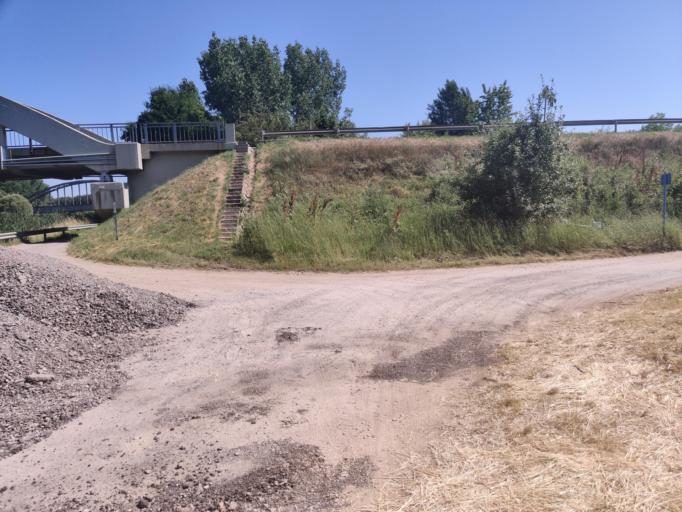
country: HU
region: Hajdu-Bihar
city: Balmazujvaros
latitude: 47.6038
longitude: 21.3795
